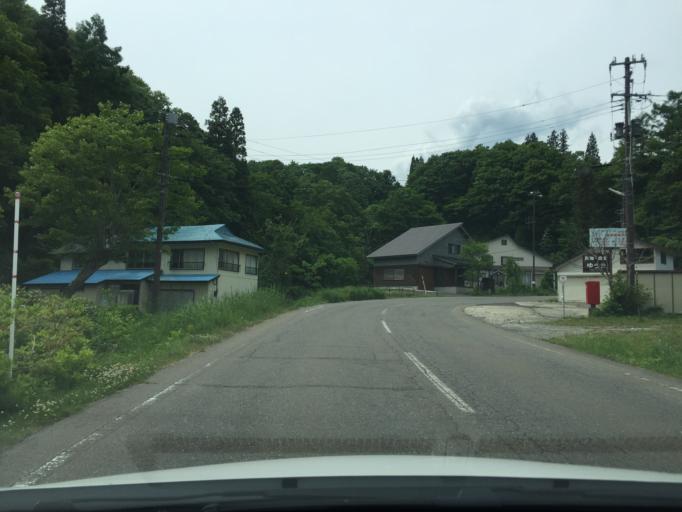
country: JP
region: Fukushima
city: Inawashiro
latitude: 37.6623
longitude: 140.0416
